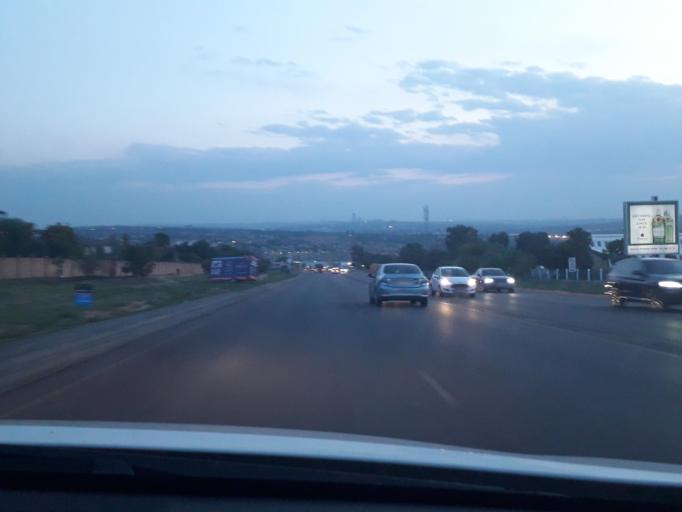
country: ZA
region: Gauteng
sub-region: City of Johannesburg Metropolitan Municipality
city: Midrand
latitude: -25.9924
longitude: 28.0766
